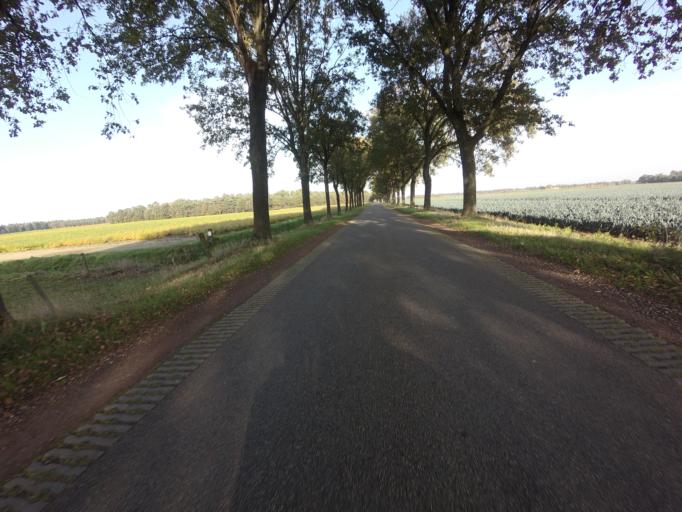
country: NL
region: Limburg
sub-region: Gemeente Roerdalen
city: Montfort
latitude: 51.1020
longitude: 5.9390
